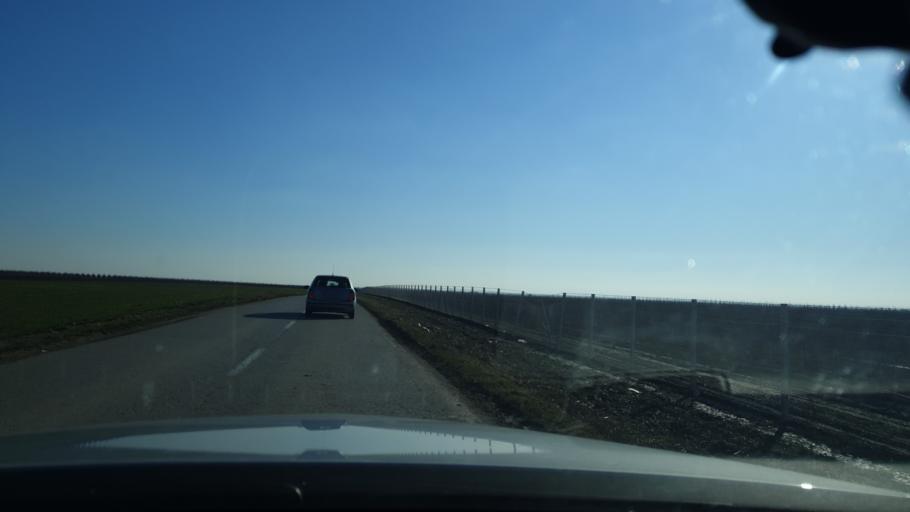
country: RS
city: Vrdnik
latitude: 45.0671
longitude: 19.8088
